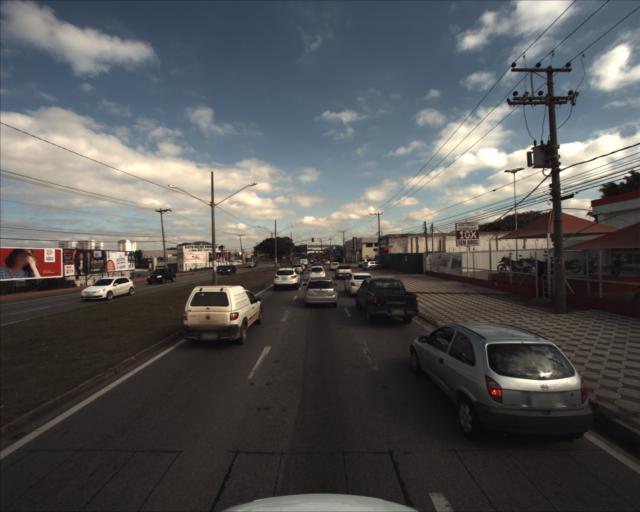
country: BR
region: Sao Paulo
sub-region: Sorocaba
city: Sorocaba
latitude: -23.5206
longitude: -47.4910
